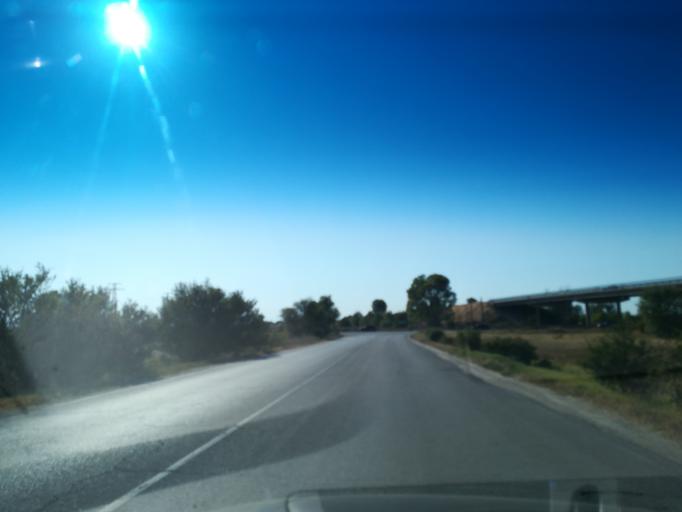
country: BG
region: Plovdiv
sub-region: Obshtina Plovdiv
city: Plovdiv
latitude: 42.1720
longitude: 24.8213
